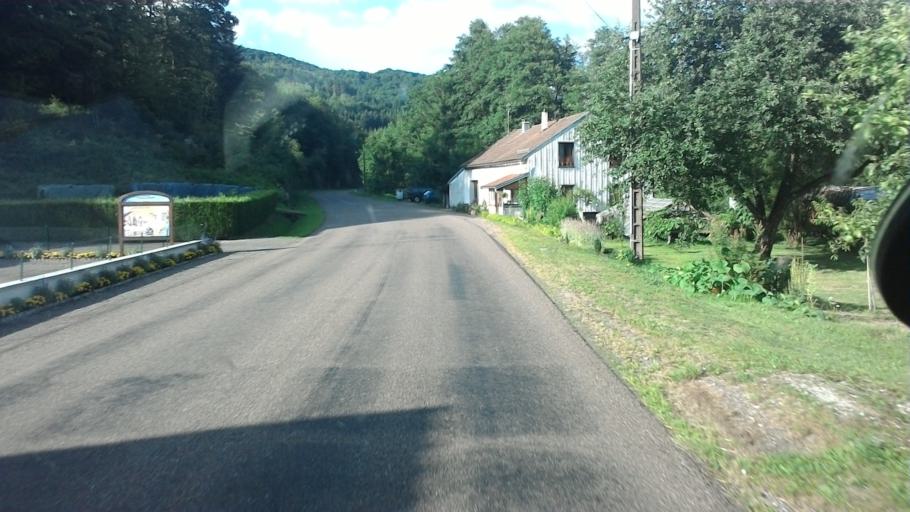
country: FR
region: Lorraine
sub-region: Departement des Vosges
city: Rupt-sur-Moselle
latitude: 47.8751
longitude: 6.5755
